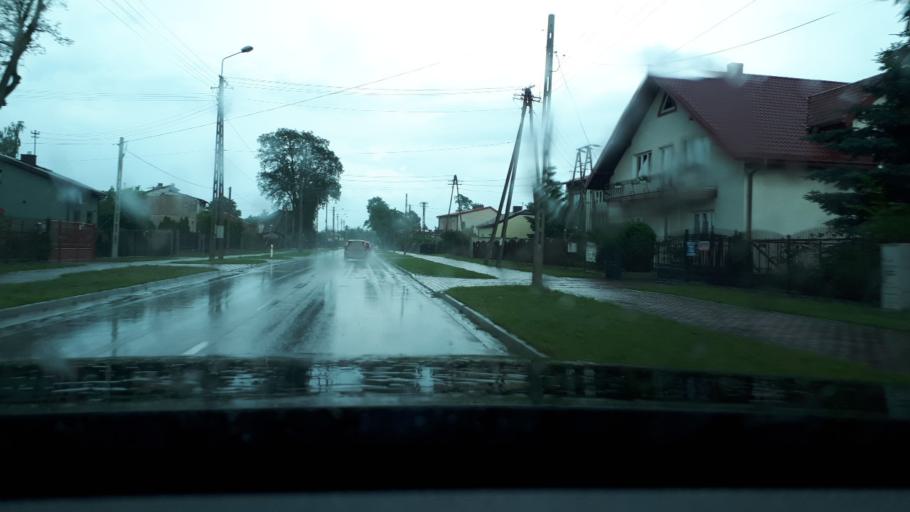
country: PL
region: Masovian Voivodeship
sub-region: Powiat warszawski zachodni
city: Jozefow
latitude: 52.2547
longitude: 20.7239
